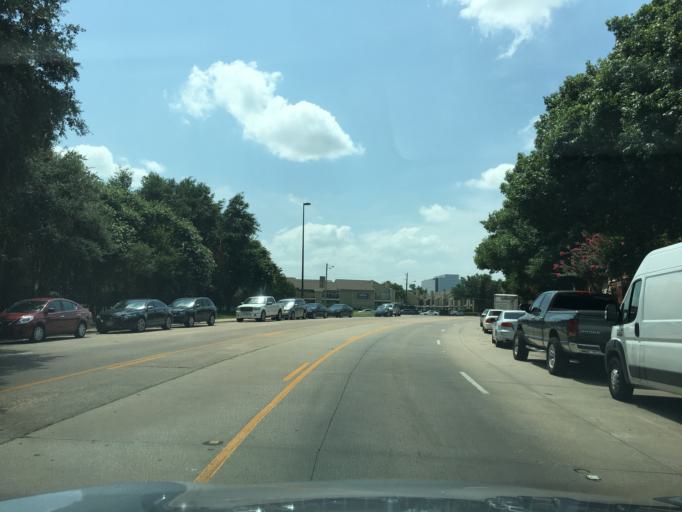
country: US
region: Texas
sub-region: Dallas County
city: Addison
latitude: 32.9431
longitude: -96.8166
